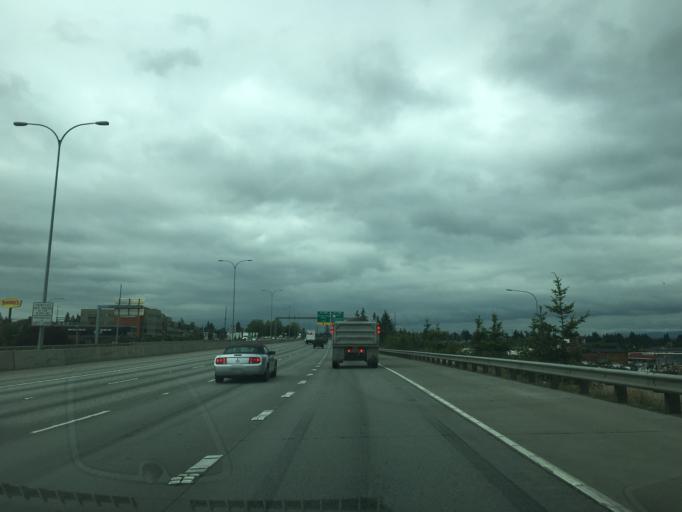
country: US
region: Washington
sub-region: Snohomish County
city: Everett
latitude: 47.9746
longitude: -122.1908
